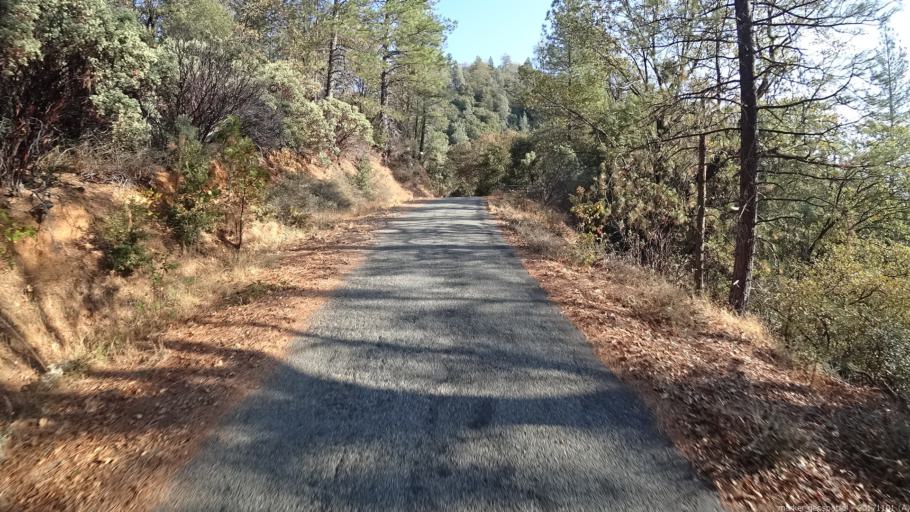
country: US
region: California
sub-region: Shasta County
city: Shasta Lake
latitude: 40.8097
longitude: -122.3164
